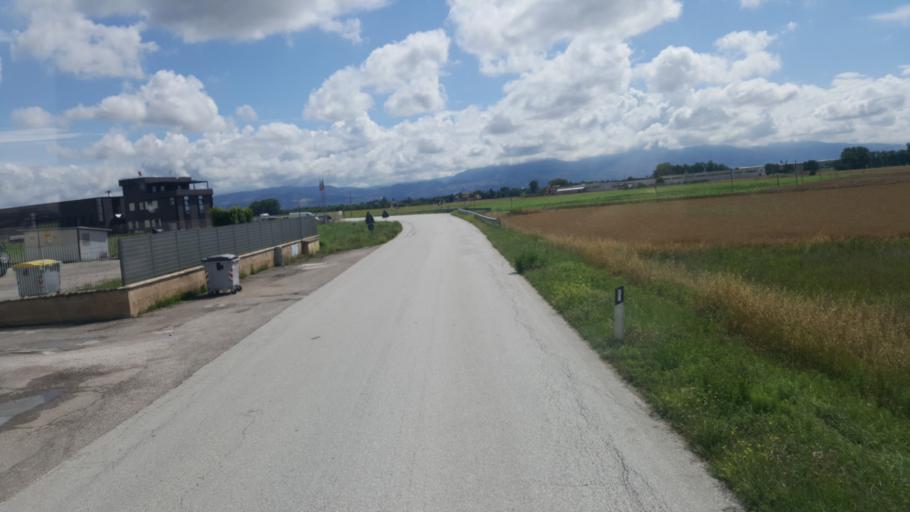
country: IT
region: Umbria
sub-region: Provincia di Perugia
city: Bettona
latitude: 43.0398
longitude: 12.4751
